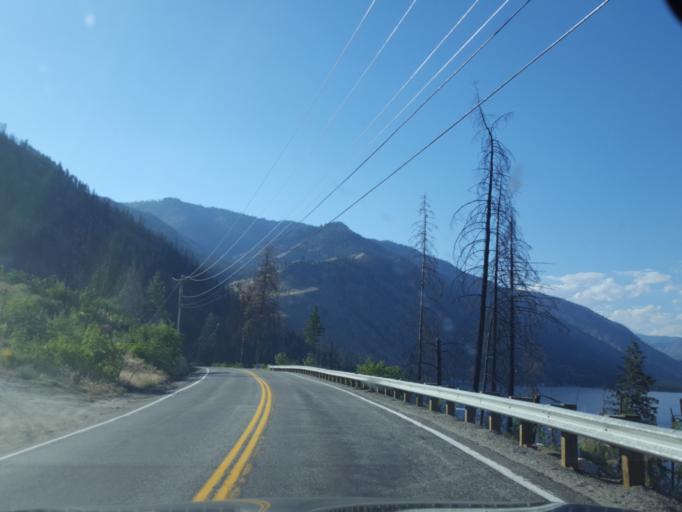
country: US
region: Washington
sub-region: Chelan County
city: Granite Falls
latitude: 47.8783
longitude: -120.2037
